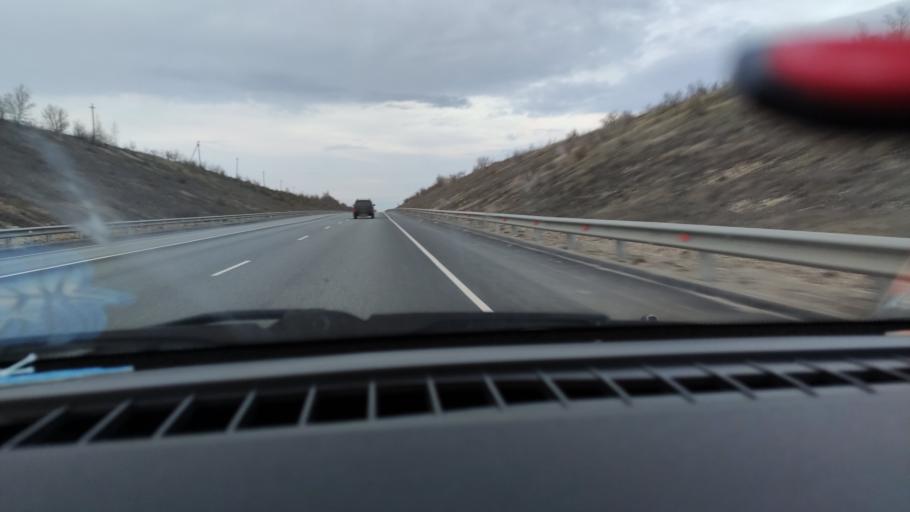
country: RU
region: Saratov
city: Yelshanka
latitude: 51.8887
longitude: 46.5208
